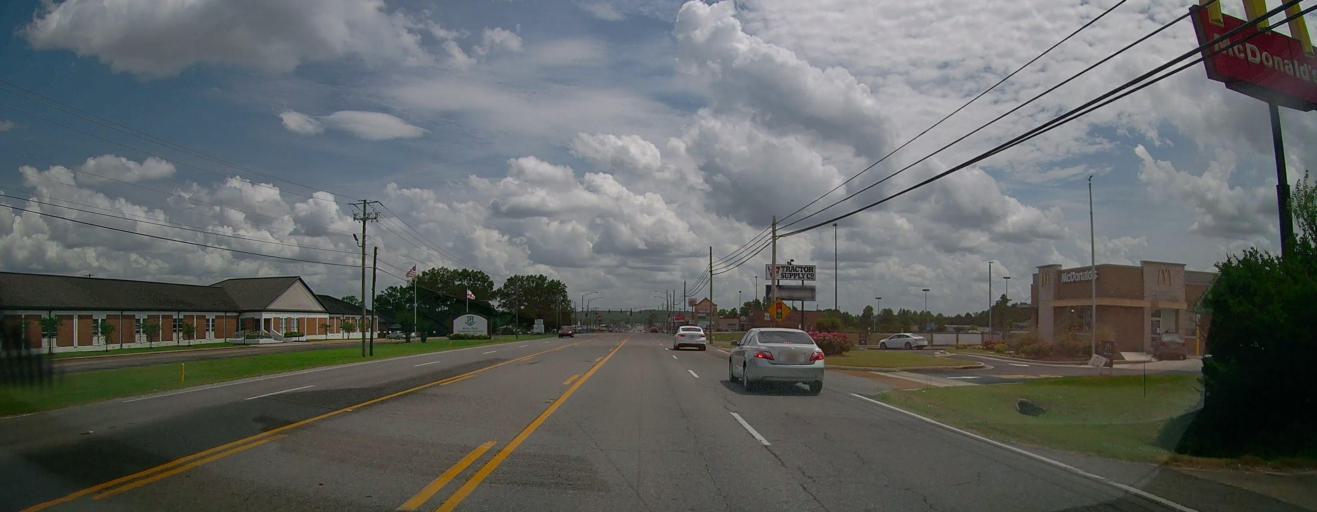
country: US
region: Alabama
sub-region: Marion County
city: Hamilton
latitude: 34.1245
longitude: -87.9898
